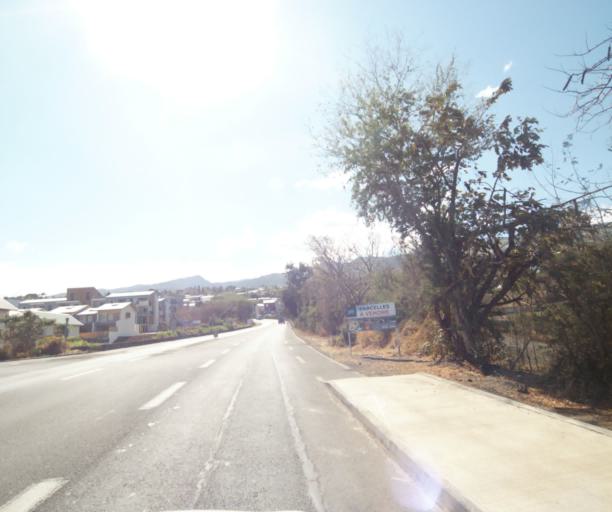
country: RE
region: Reunion
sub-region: Reunion
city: Le Port
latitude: -20.9810
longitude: 55.3154
